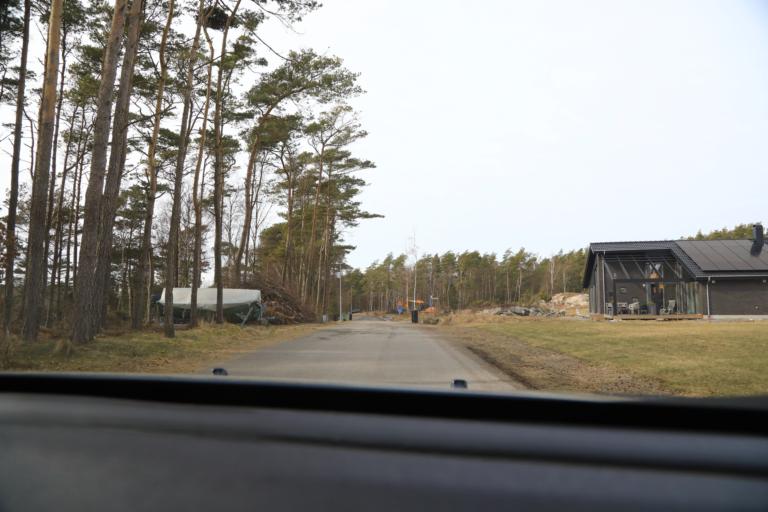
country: SE
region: Halland
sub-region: Kungsbacka Kommun
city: Frillesas
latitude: 57.2311
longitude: 12.1152
